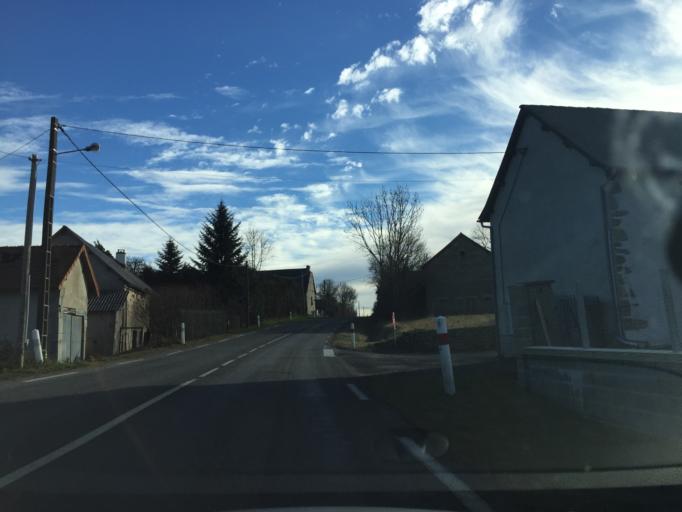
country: FR
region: Limousin
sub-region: Departement de la Creuse
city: Auzances
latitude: 45.8763
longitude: 2.5089
